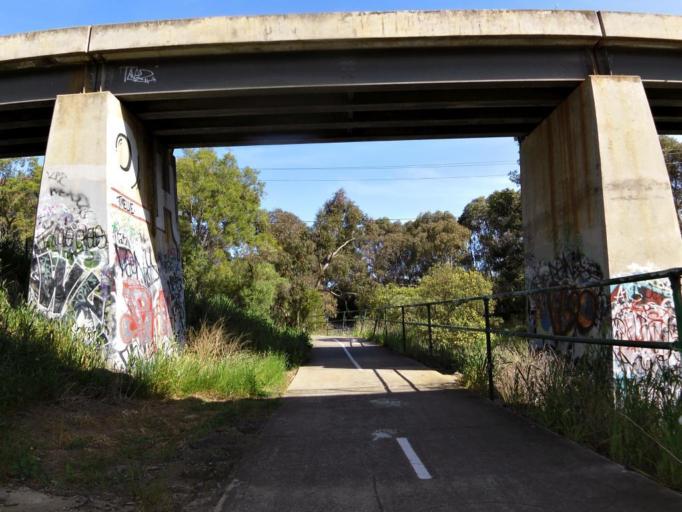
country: AU
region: Victoria
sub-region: Brimbank
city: Sunshine West
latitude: -37.7843
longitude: 144.8154
